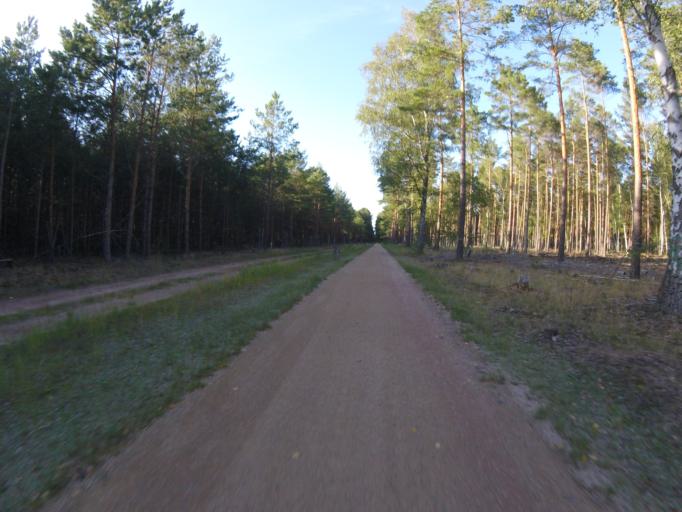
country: DE
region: Brandenburg
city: Munchehofe
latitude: 52.1955
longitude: 13.7636
